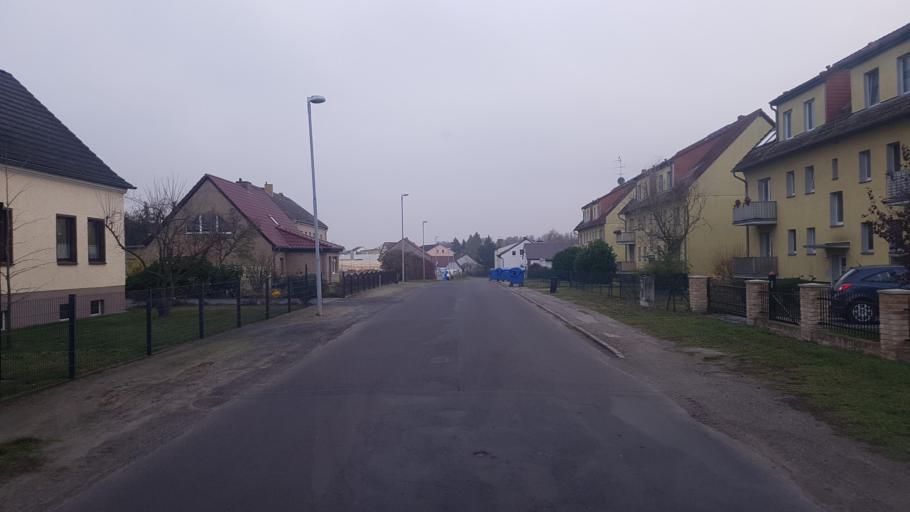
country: DE
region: Brandenburg
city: Roskow
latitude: 52.4220
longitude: 12.7154
